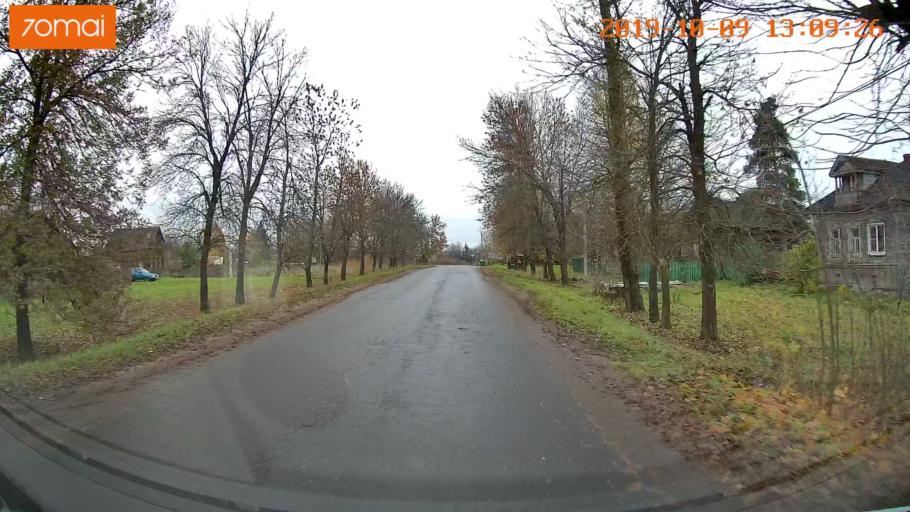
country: RU
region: Jaroslavl
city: Lyubim
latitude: 58.3560
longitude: 40.6751
